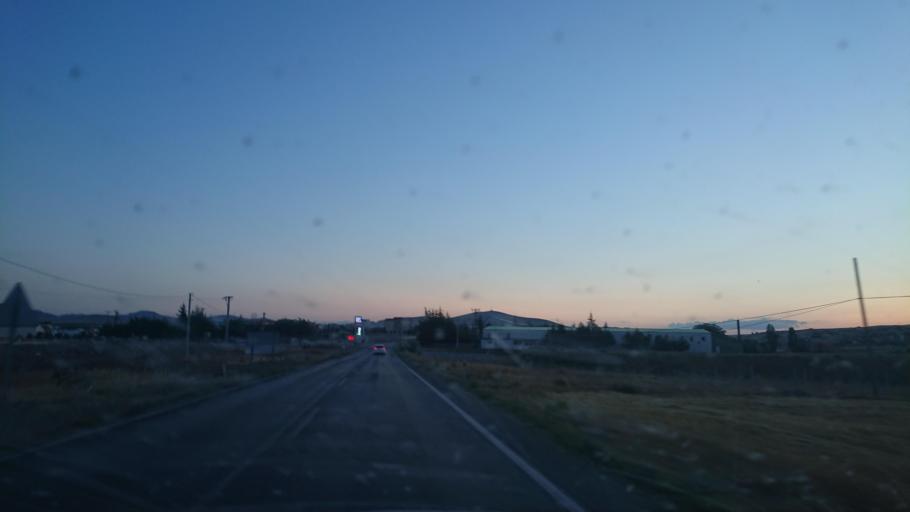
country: TR
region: Aksaray
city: Balci
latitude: 38.7589
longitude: 34.0814
